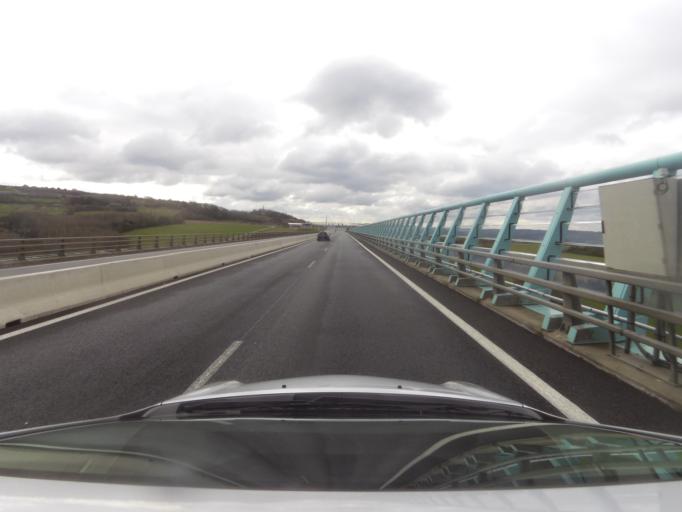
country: FR
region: Nord-Pas-de-Calais
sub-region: Departement du Pas-de-Calais
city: Saint-Leonard
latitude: 50.6948
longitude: 1.6374
